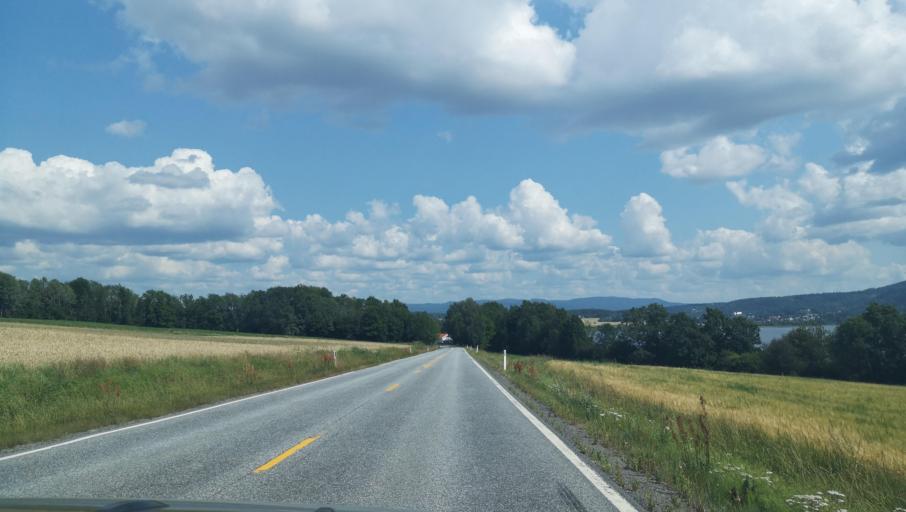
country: NO
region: Buskerud
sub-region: Ovre Eiker
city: Hokksund
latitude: 59.7071
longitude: 9.8126
